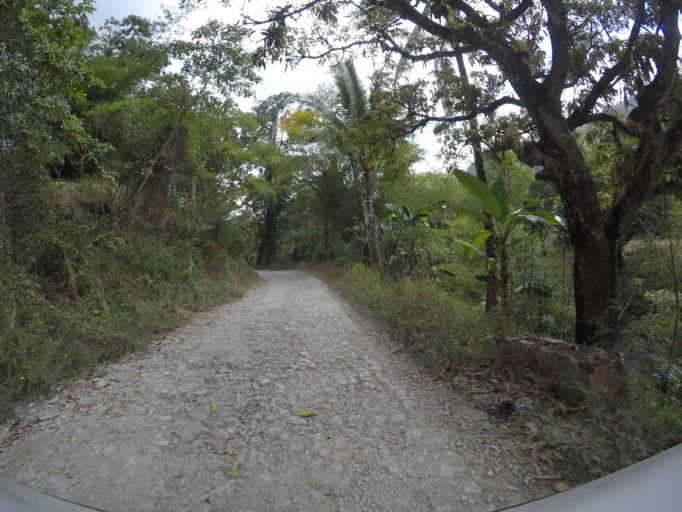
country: TL
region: Baucau
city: Baucau
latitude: -8.6247
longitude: 126.6564
